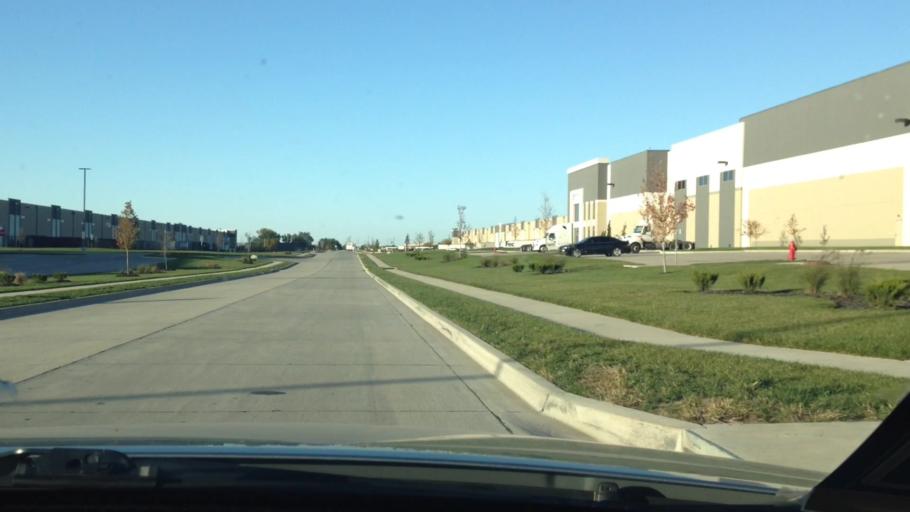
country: US
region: Kansas
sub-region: Johnson County
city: Gardner
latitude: 38.7753
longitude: -94.9423
